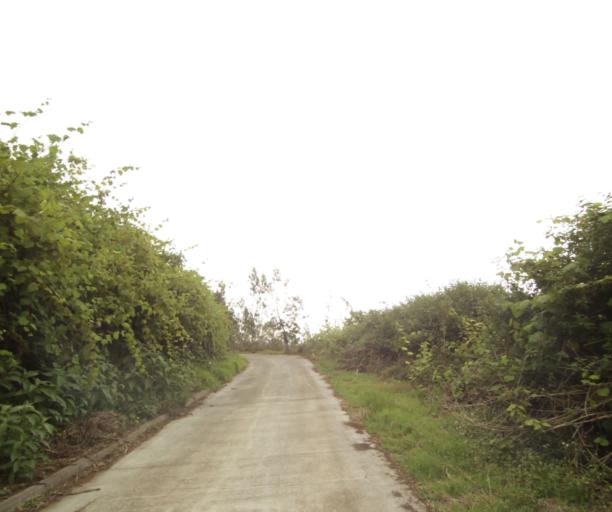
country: RE
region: Reunion
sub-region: Reunion
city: Saint-Paul
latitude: -21.0161
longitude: 55.3549
